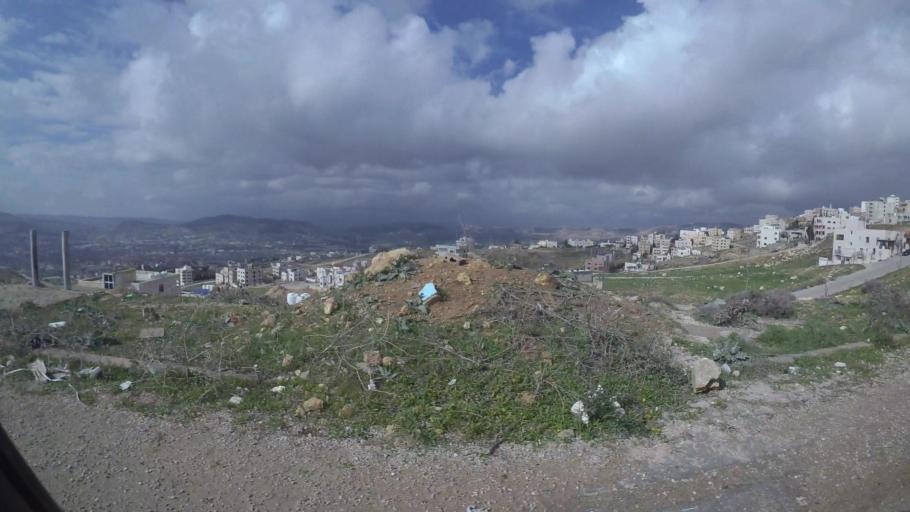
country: JO
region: Amman
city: Al Jubayhah
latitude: 32.0577
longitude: 35.8642
